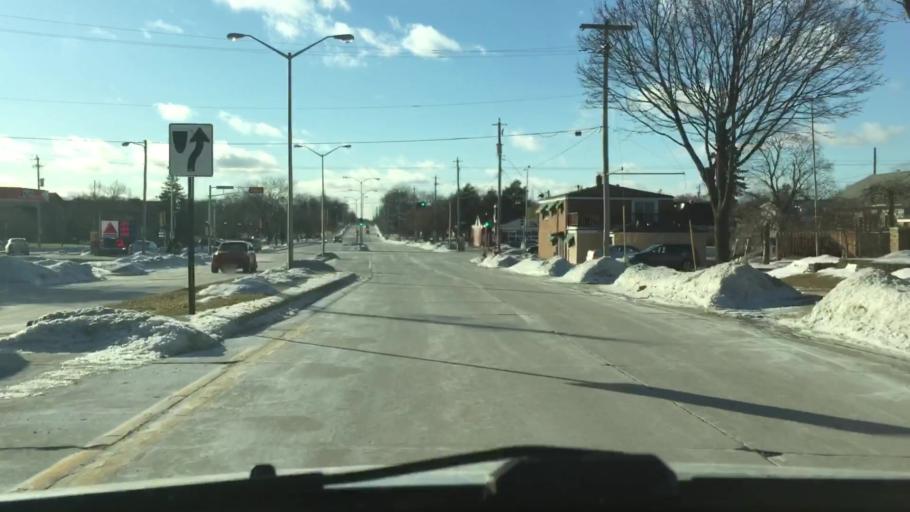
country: US
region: Wisconsin
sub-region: Milwaukee County
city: Greenfield
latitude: 42.9738
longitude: -88.0266
